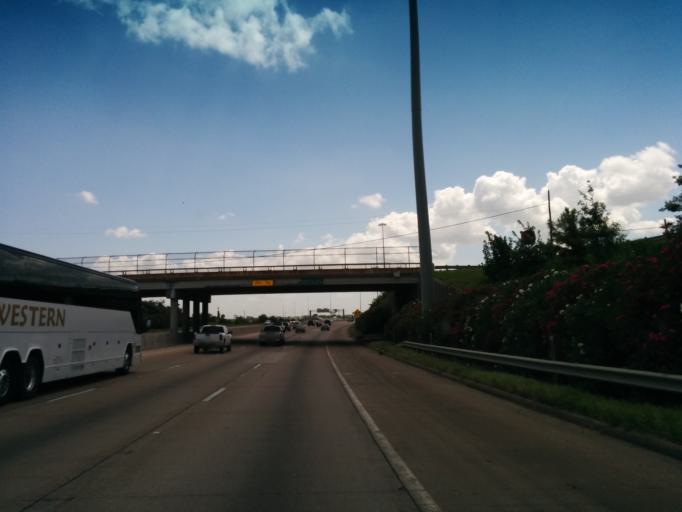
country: US
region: Texas
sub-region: Harris County
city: Channelview
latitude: 29.7902
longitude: -95.0903
